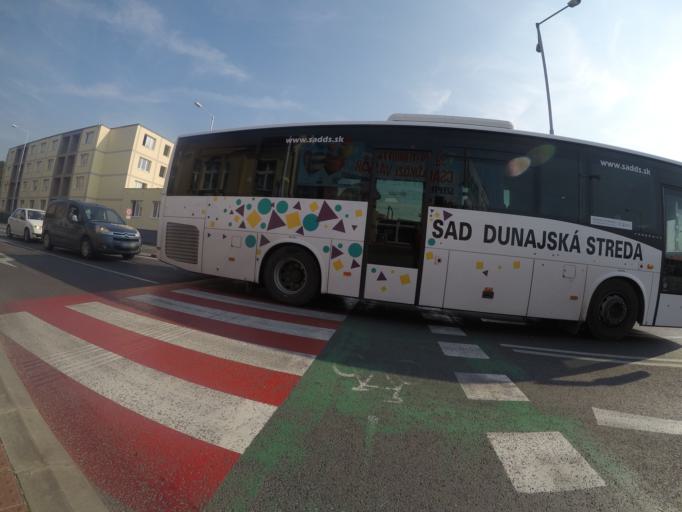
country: SK
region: Trnavsky
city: Dunajska Streda
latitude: 47.9916
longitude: 17.6202
